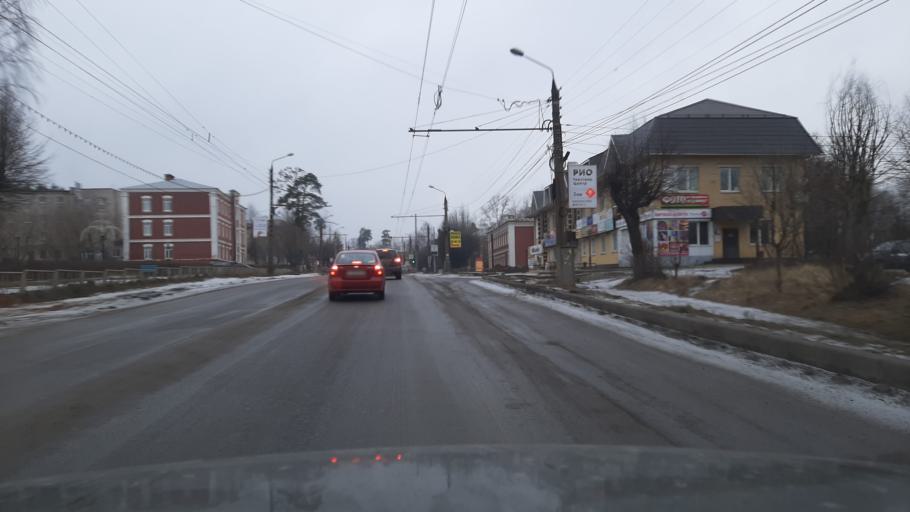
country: RU
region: Ivanovo
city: Kokhma
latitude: 56.9319
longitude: 41.0788
